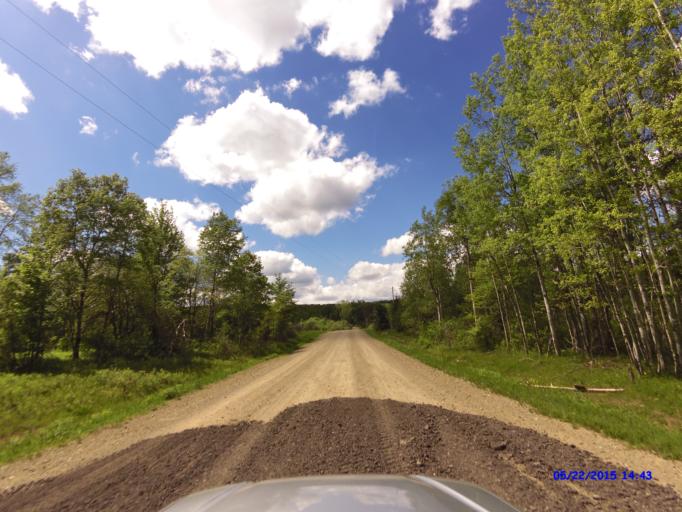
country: US
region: New York
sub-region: Cattaraugus County
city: Franklinville
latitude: 42.3542
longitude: -78.5614
